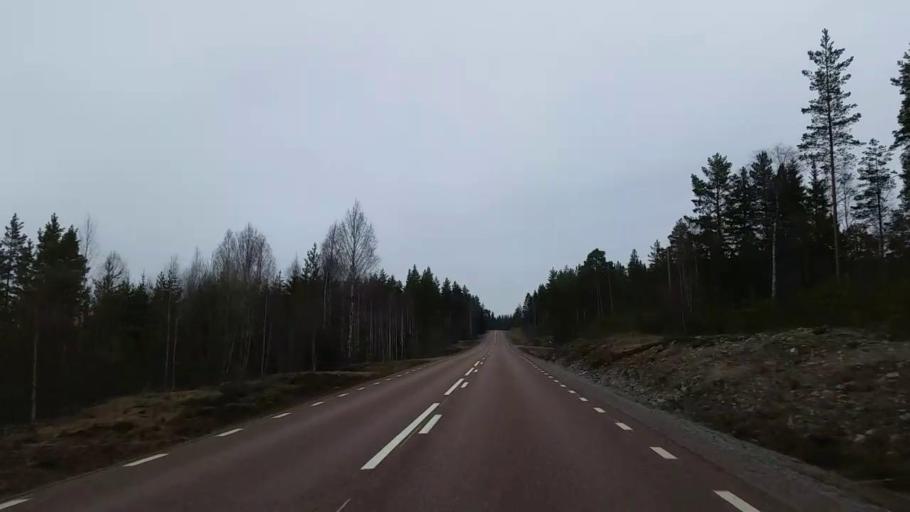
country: SE
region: Gaevleborg
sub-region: Ovanakers Kommun
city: Edsbyn
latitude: 61.2203
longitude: 15.8770
